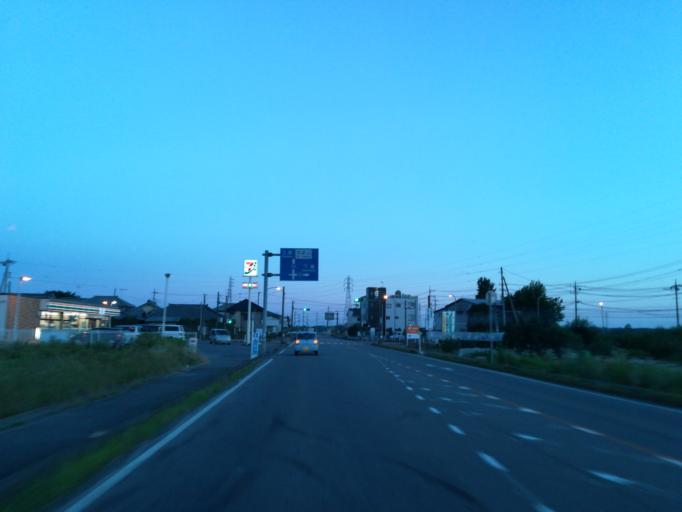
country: JP
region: Ibaraki
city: Tsukuba
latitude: 36.2238
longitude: 140.0646
